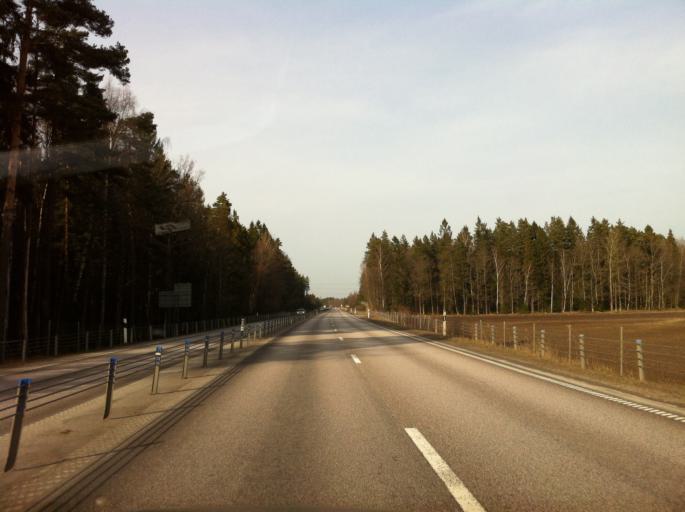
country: SE
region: Vaestra Goetaland
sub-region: Skovde Kommun
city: Stopen
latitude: 58.5025
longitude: 13.8408
